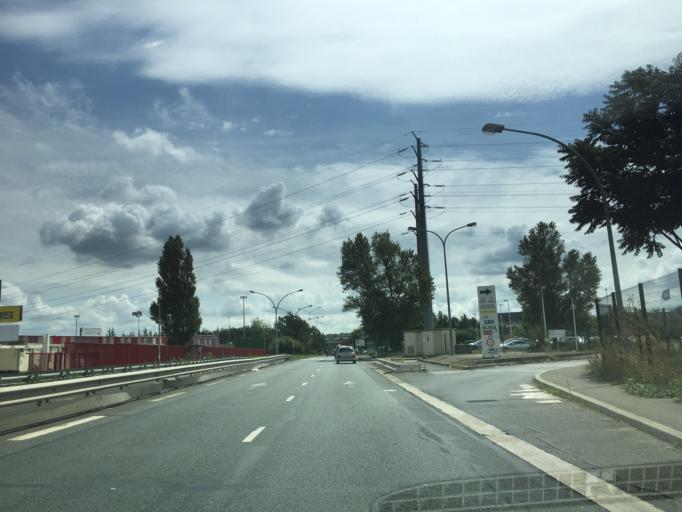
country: FR
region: Ile-de-France
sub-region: Departement du Val-de-Marne
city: Bonneuil-sur-Marne
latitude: 48.7604
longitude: 2.4795
